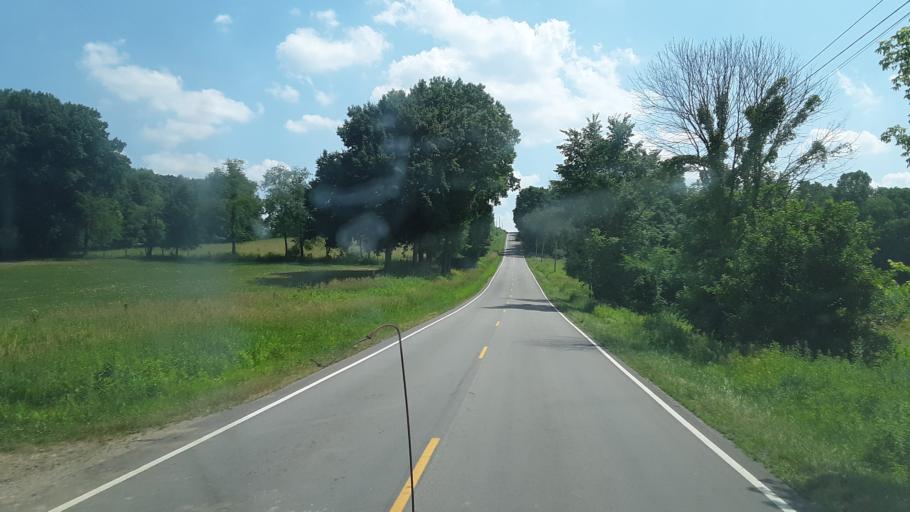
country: US
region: Ohio
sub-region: Stark County
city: Navarre
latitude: 40.6804
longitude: -81.4721
